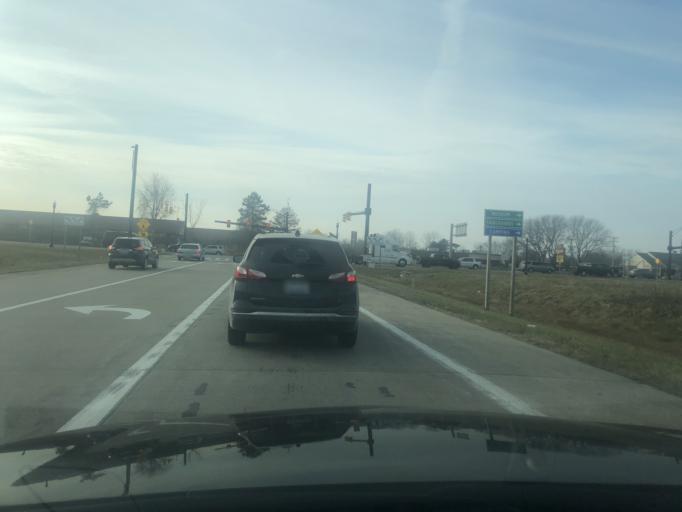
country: US
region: Michigan
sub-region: Wayne County
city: Belleville
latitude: 42.2217
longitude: -83.4842
